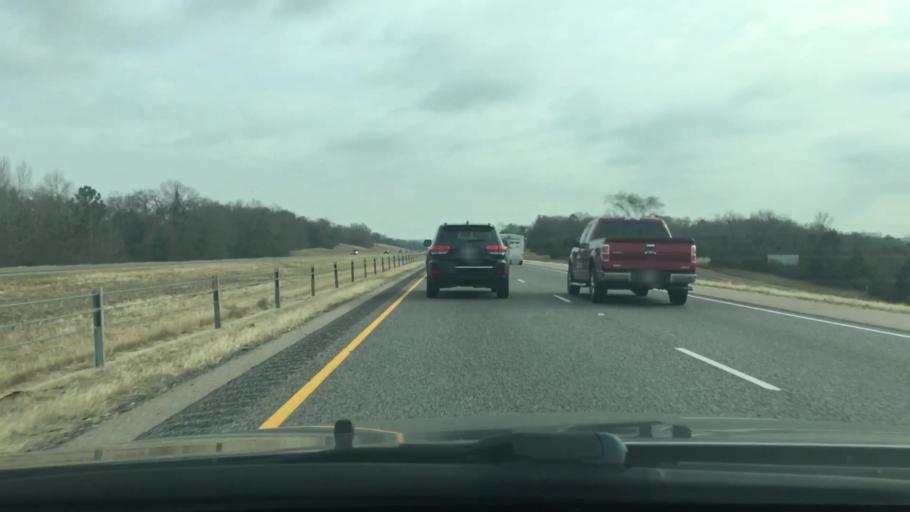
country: US
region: Texas
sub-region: Leon County
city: Buffalo
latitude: 31.5217
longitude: -96.1107
